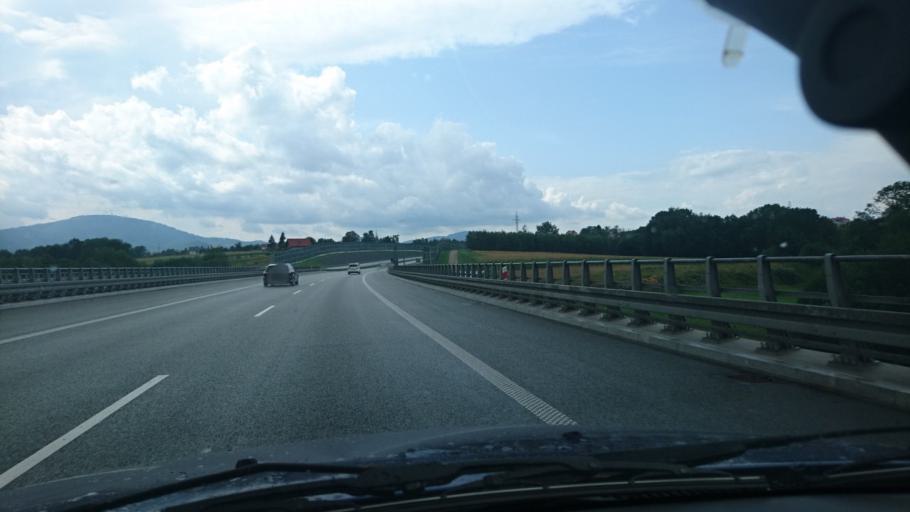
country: PL
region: Silesian Voivodeship
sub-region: Powiat zywiecki
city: Pietrzykowice
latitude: 49.6853
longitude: 19.1459
